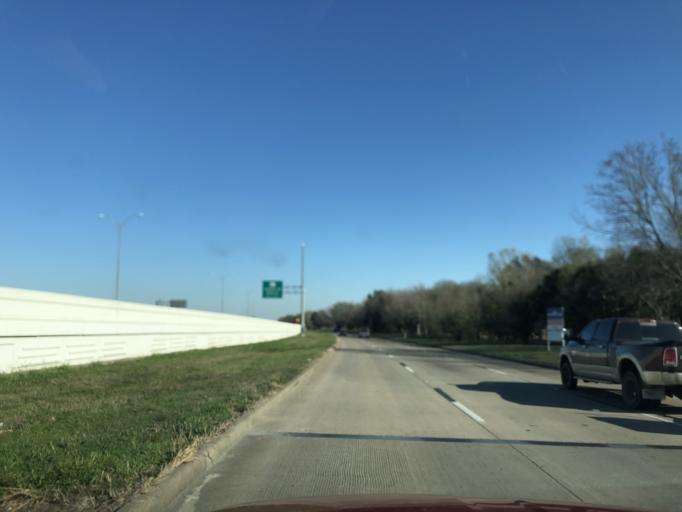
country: US
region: Texas
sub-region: Fort Bend County
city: Fresno
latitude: 29.5966
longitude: -95.4564
